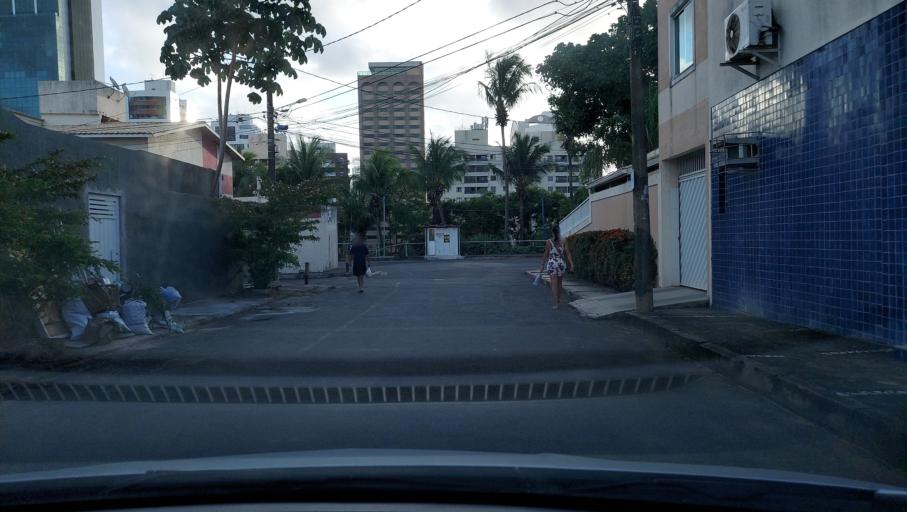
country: BR
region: Bahia
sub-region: Salvador
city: Salvador
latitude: -12.9851
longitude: -38.4475
